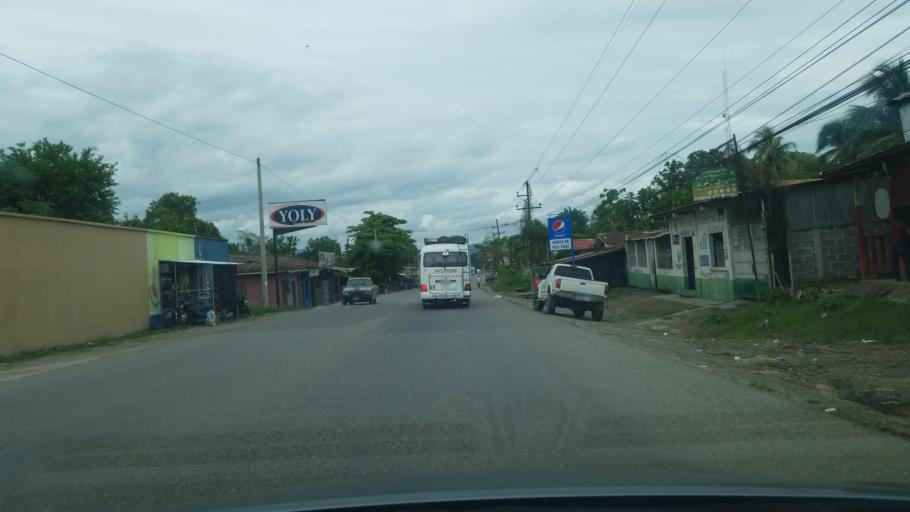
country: HN
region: Santa Barbara
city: El Ciruelo
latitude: 15.2944
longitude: -88.4892
